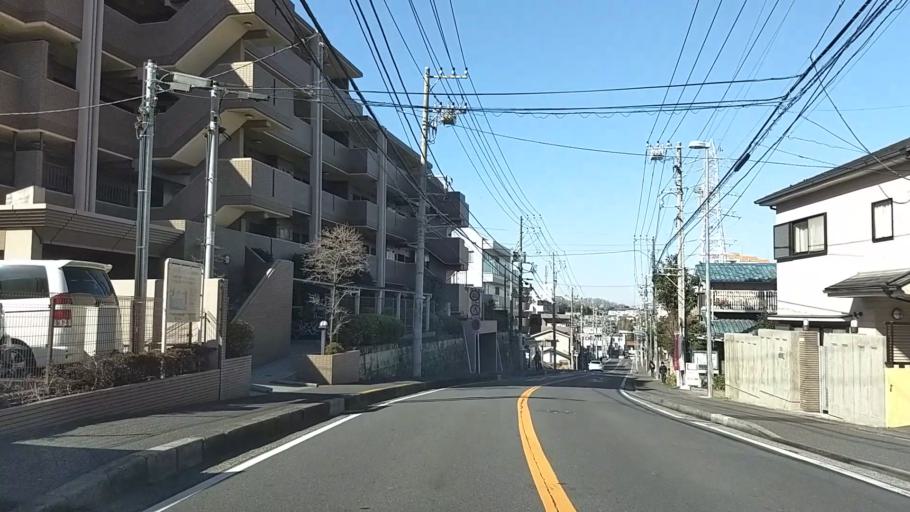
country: JP
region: Kanagawa
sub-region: Kawasaki-shi
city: Kawasaki
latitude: 35.5151
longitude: 139.6506
